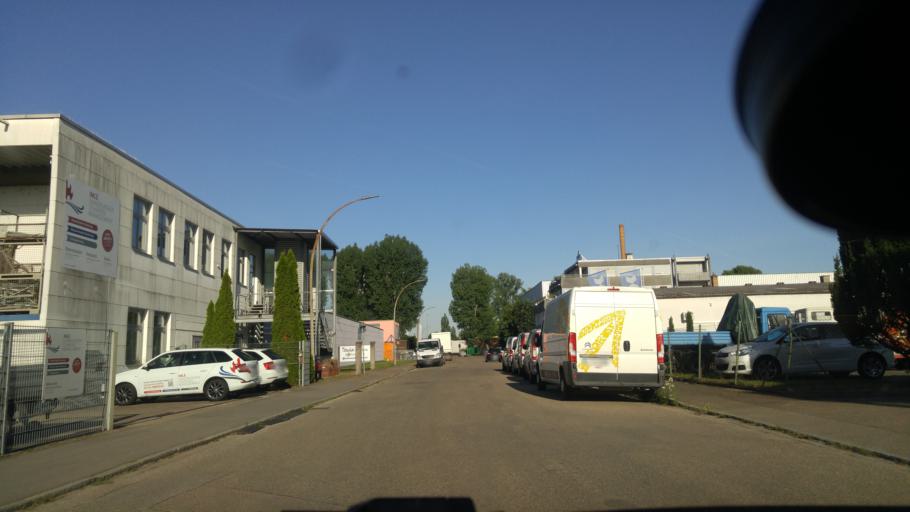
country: DE
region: Baden-Wuerttemberg
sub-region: Regierungsbezirk Stuttgart
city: Weinstadt-Endersbach
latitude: 48.8158
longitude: 9.3723
